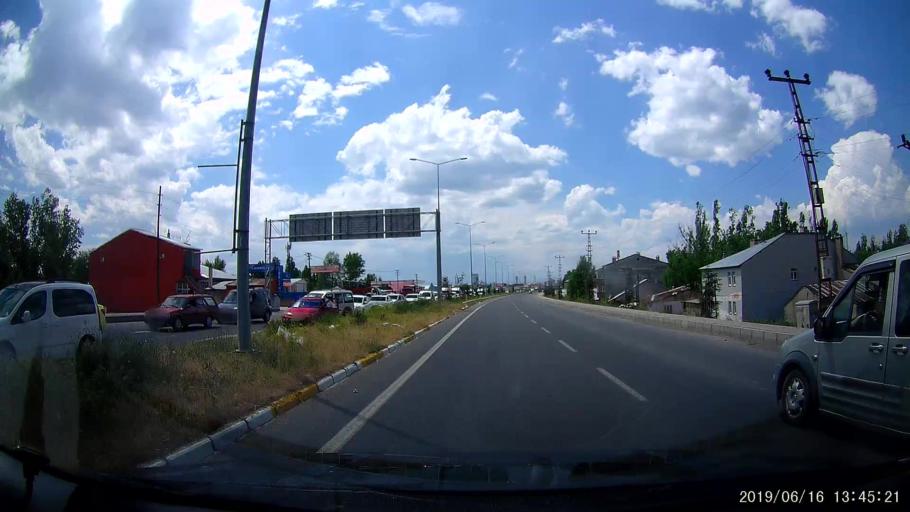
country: TR
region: Agri
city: Agri
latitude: 39.7086
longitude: 43.0468
